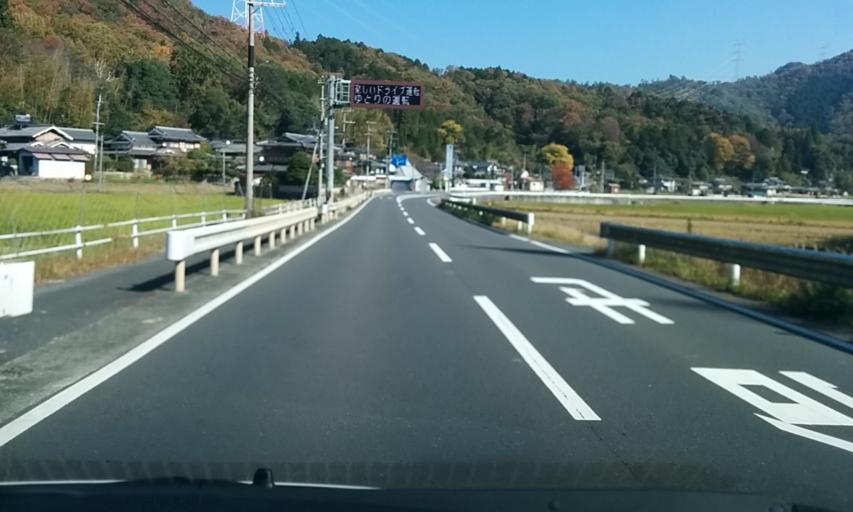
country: JP
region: Kyoto
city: Kameoka
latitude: 35.1349
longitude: 135.4879
